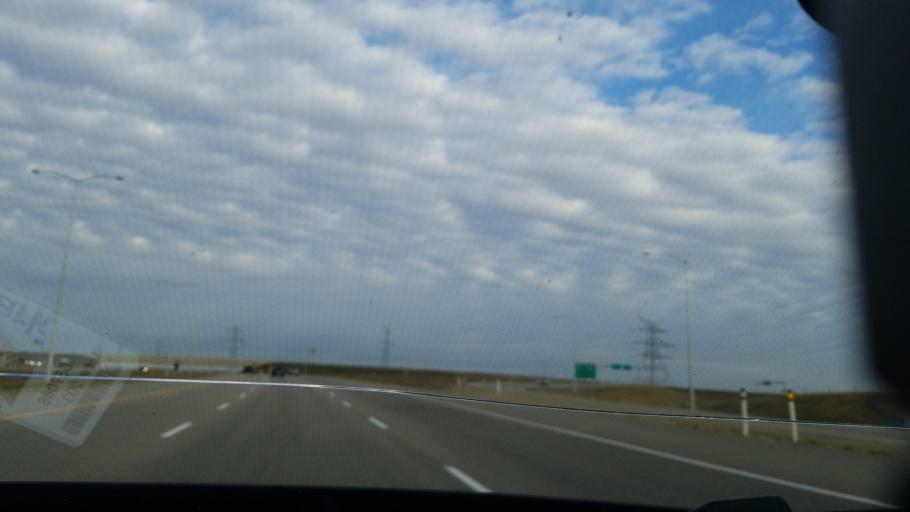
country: CA
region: Alberta
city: Sherwood Park
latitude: 53.6132
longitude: -113.3555
